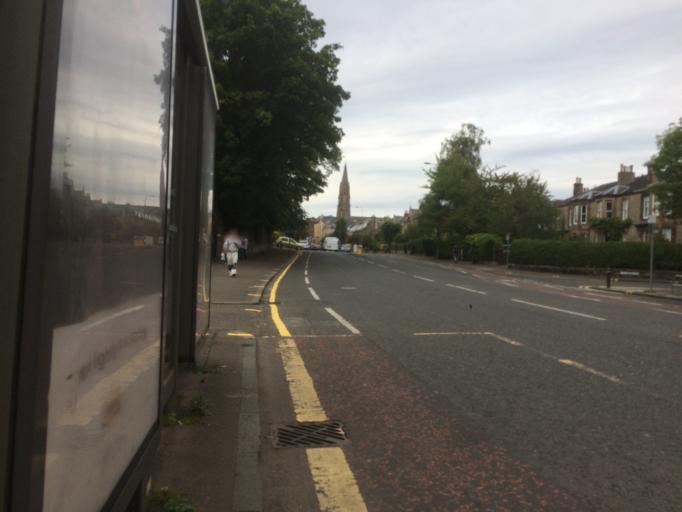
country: GB
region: Scotland
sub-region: Edinburgh
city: Edinburgh
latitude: 55.9304
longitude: -3.1763
